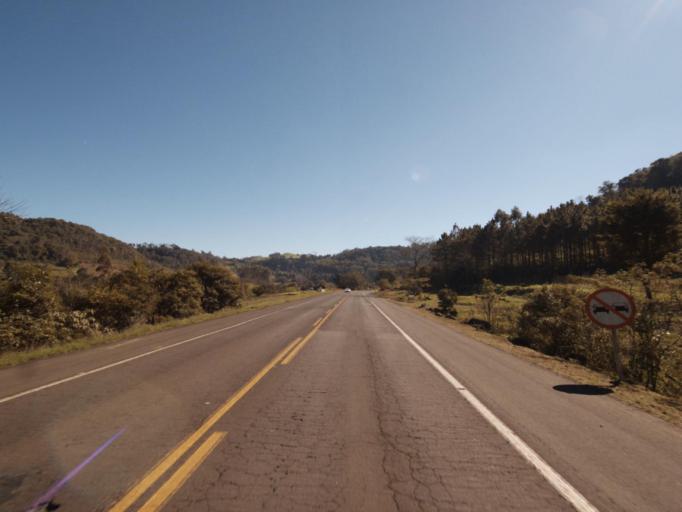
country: BR
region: Rio Grande do Sul
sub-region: Frederico Westphalen
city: Frederico Westphalen
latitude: -26.9718
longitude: -53.2156
